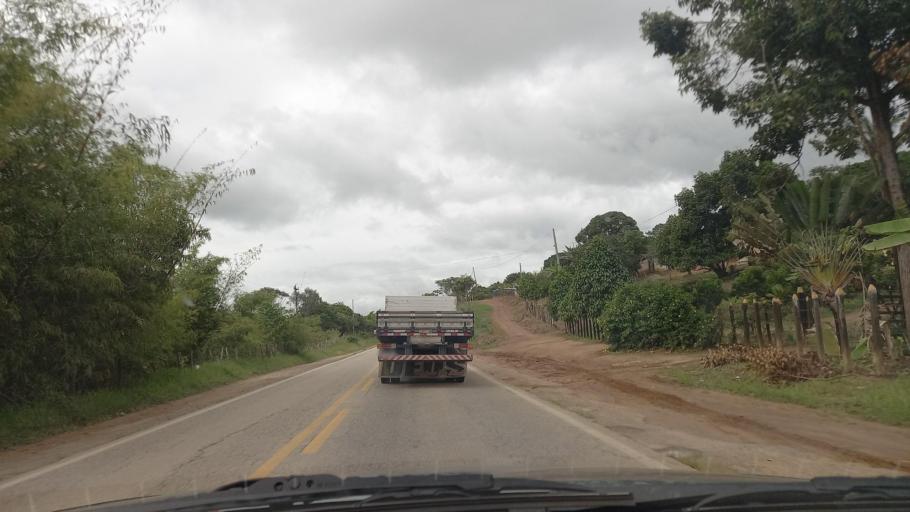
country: BR
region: Pernambuco
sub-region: Canhotinho
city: Canhotinho
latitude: -8.8566
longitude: -36.1742
